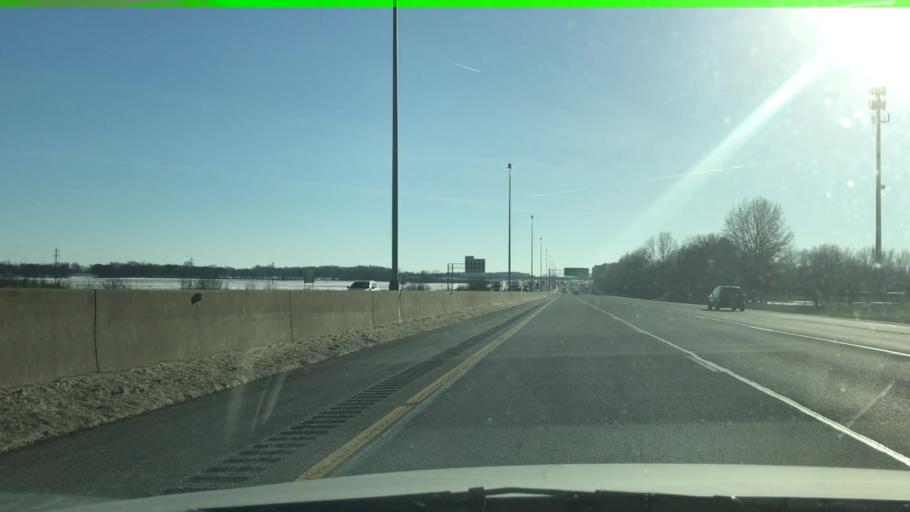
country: US
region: Kentucky
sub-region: Warren County
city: Plano
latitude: 36.9227
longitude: -86.4252
